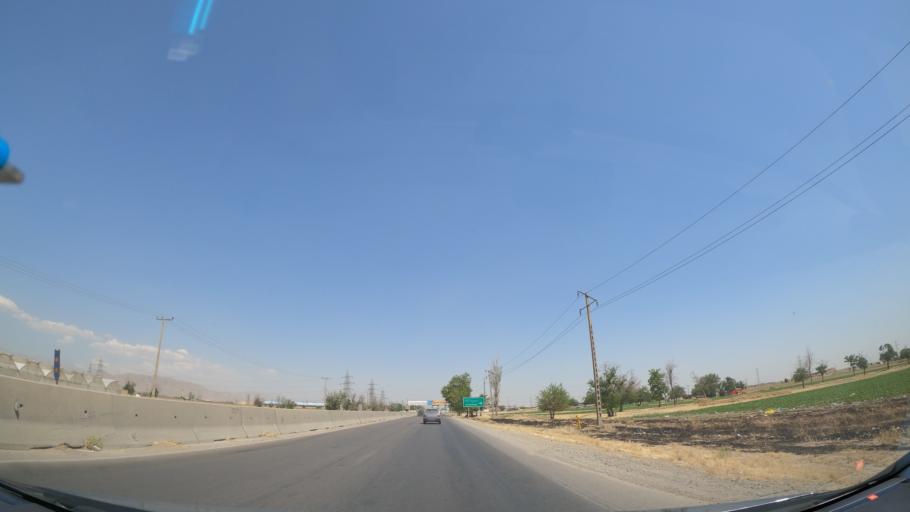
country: IR
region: Alborz
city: Hashtgerd
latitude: 35.9251
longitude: 50.7385
